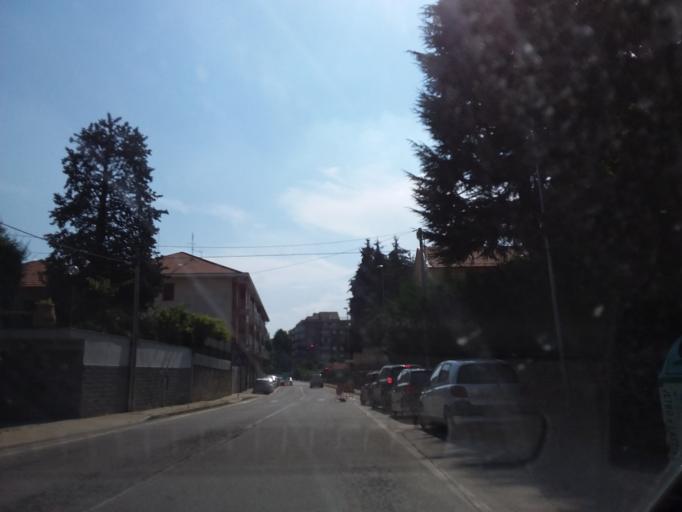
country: IT
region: Piedmont
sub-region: Provincia di Torino
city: Rivoli
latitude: 45.0753
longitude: 7.5417
